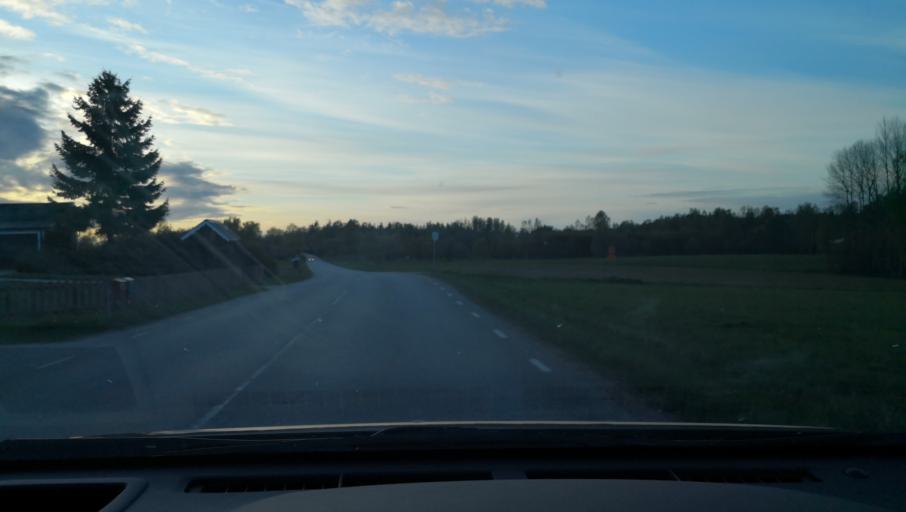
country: SE
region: OErebro
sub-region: Askersunds Kommun
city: Asbro
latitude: 58.9294
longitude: 15.0301
